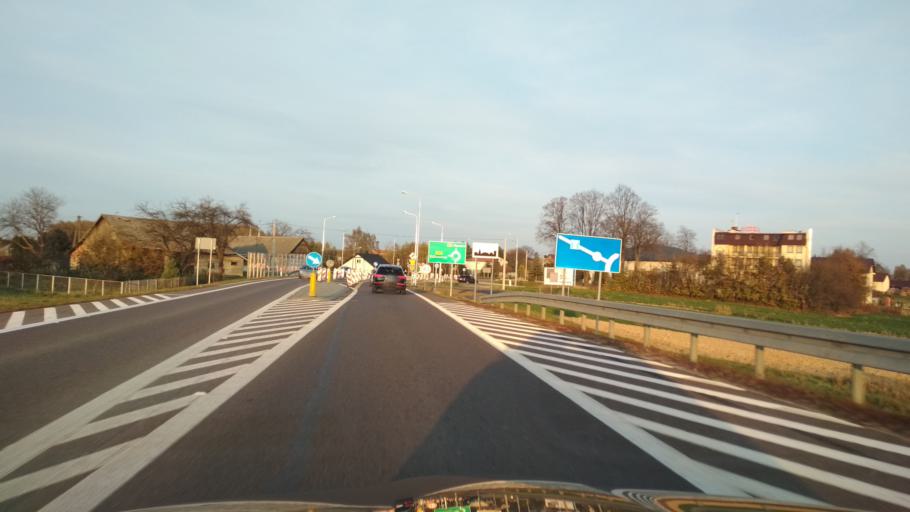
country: PL
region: Subcarpathian Voivodeship
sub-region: Powiat ropczycko-sedziszowski
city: Sedziszow Malopolski
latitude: 50.0688
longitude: 21.7396
